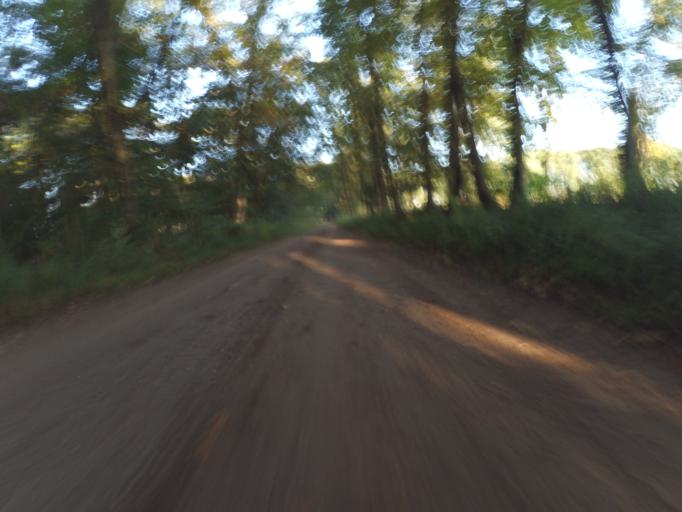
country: NL
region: Gelderland
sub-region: Gemeente Barneveld
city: Garderen
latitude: 52.2284
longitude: 5.7538
